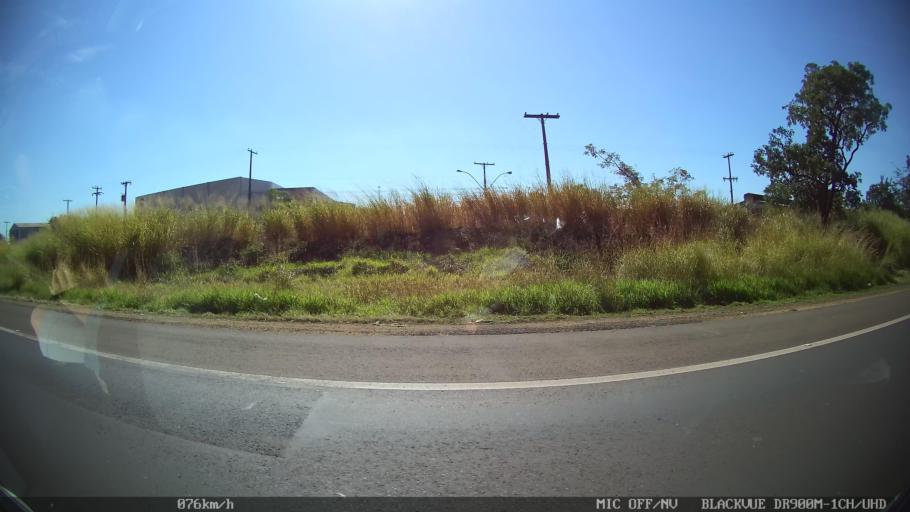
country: BR
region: Sao Paulo
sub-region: Franca
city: Franca
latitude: -20.5576
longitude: -47.4433
